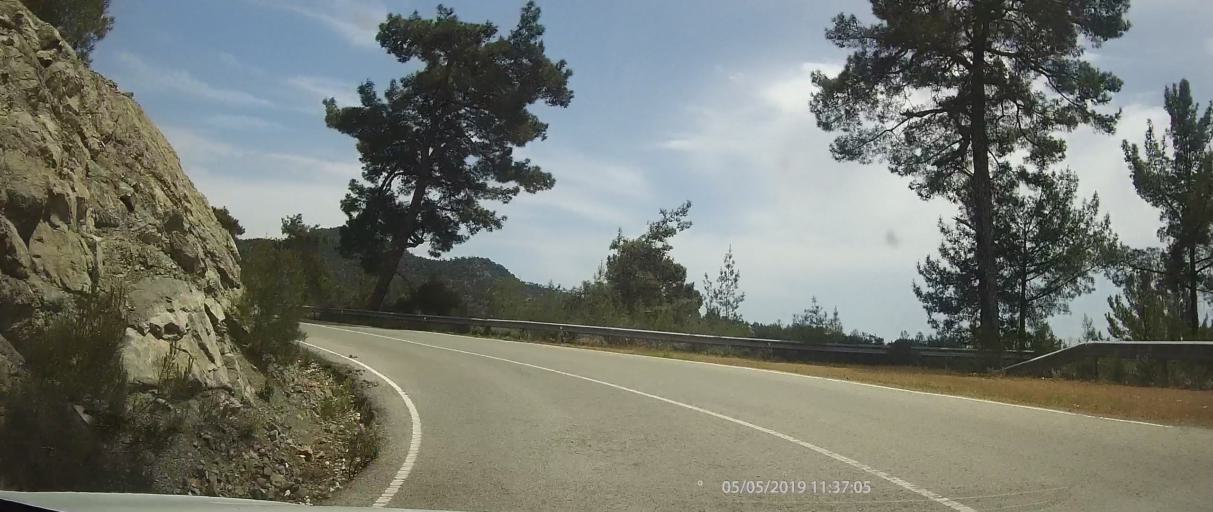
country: CY
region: Lefkosia
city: Kato Pyrgos
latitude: 34.9711
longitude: 32.6562
